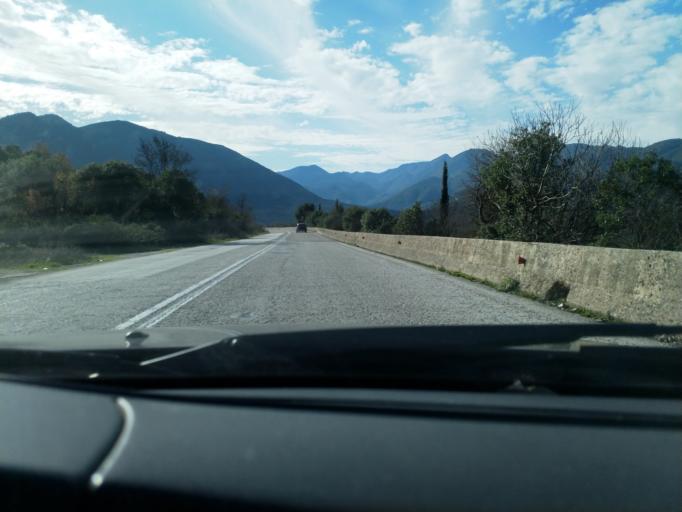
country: GR
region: Epirus
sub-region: Nomos Ioanninon
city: Agia Kyriaki
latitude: 39.4689
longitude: 20.8767
